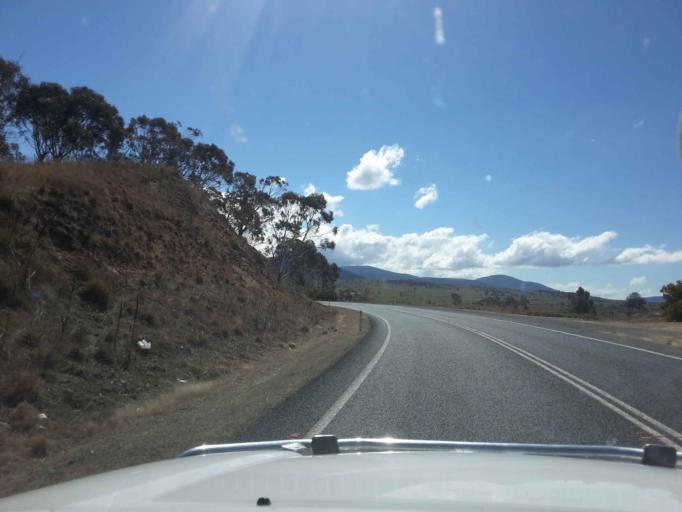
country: AU
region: New South Wales
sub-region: Snowy River
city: Jindabyne
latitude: -36.4066
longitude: 148.6003
